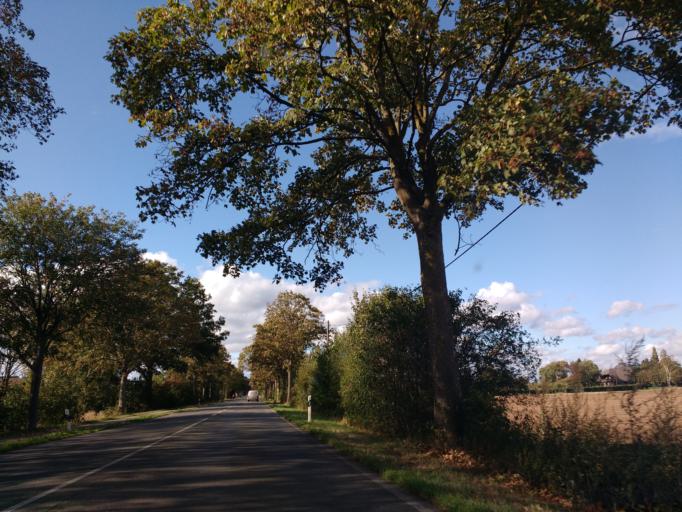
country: DE
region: North Rhine-Westphalia
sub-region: Regierungsbezirk Dusseldorf
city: Alpen
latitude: 51.6006
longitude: 6.5270
